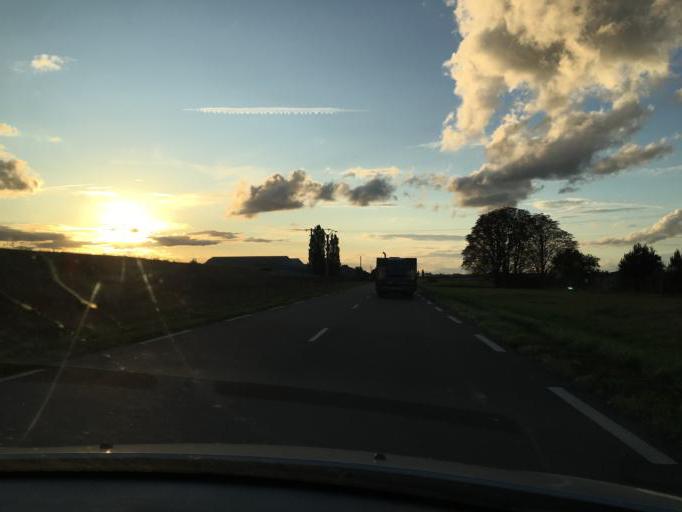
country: FR
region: Centre
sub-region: Departement d'Eure-et-Loir
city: Chateaudun
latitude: 48.0626
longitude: 1.3837
